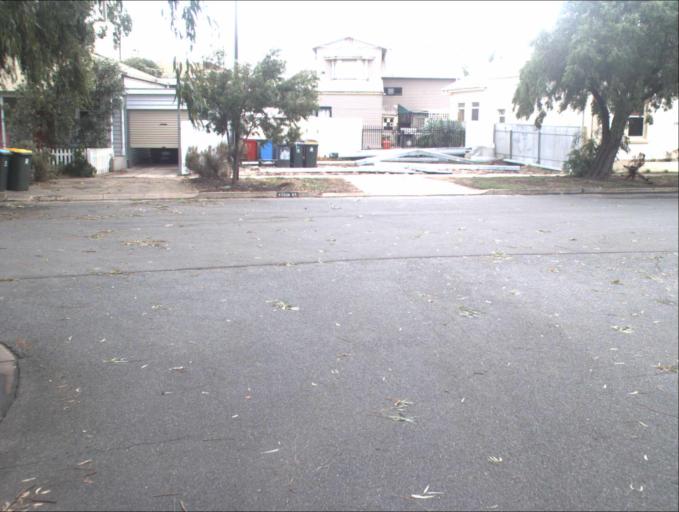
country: AU
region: South Australia
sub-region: Port Adelaide Enfield
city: Birkenhead
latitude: -34.8437
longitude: 138.4845
